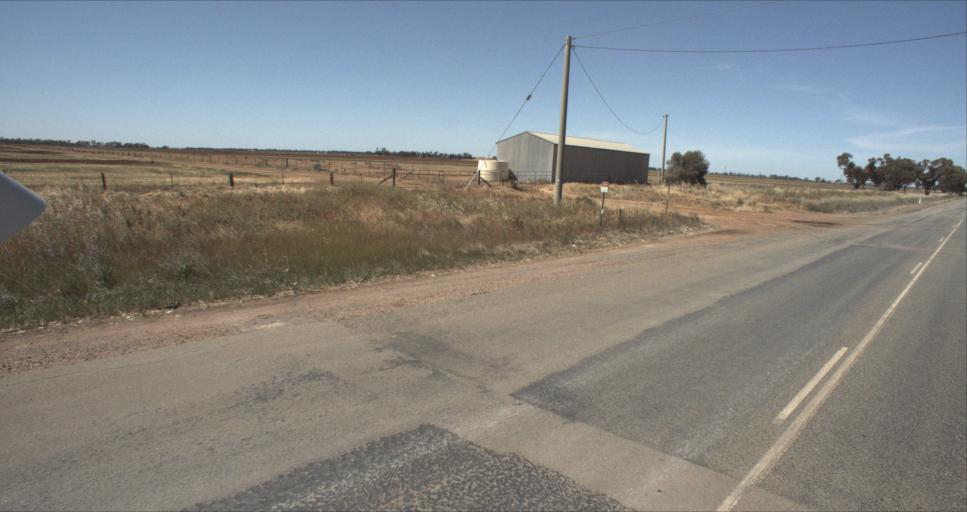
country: AU
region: New South Wales
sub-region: Leeton
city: Leeton
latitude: -34.4997
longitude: 146.2871
